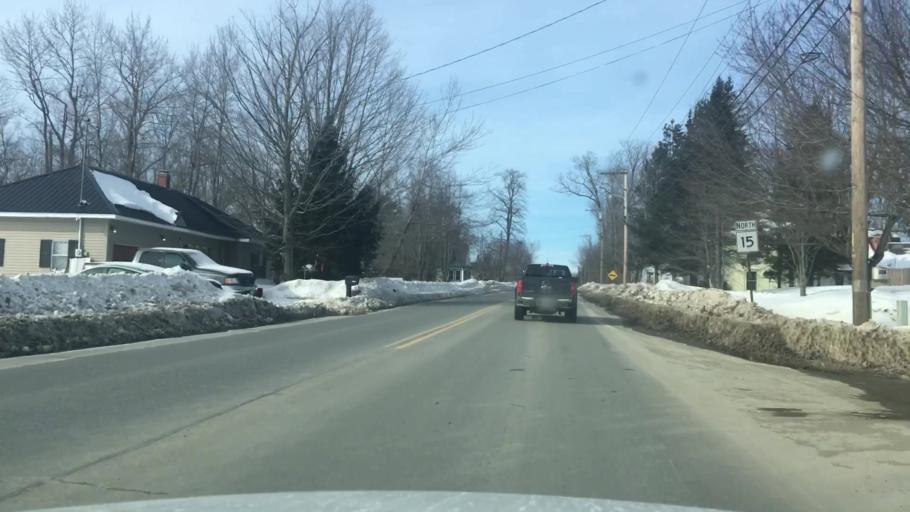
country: US
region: Maine
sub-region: Penobscot County
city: Kenduskeag
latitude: 44.9200
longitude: -68.9312
